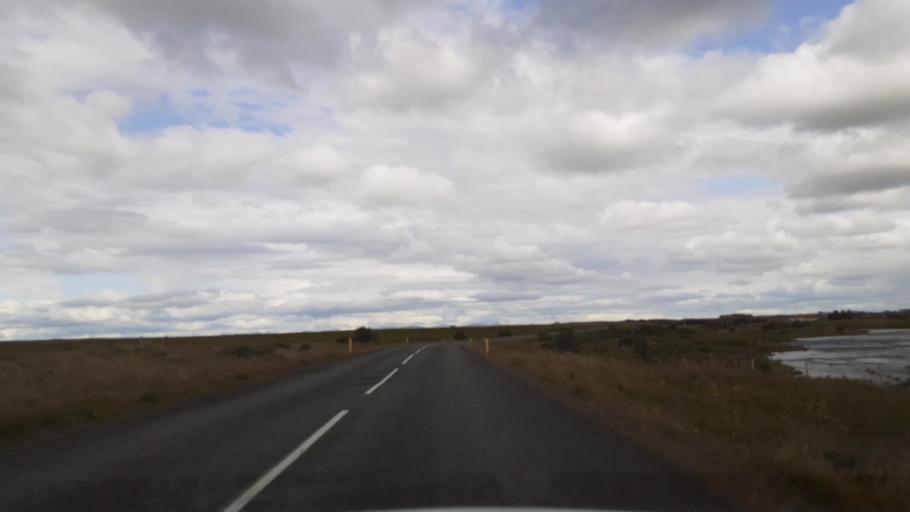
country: IS
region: South
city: Vestmannaeyjar
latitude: 63.8243
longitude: -20.4276
